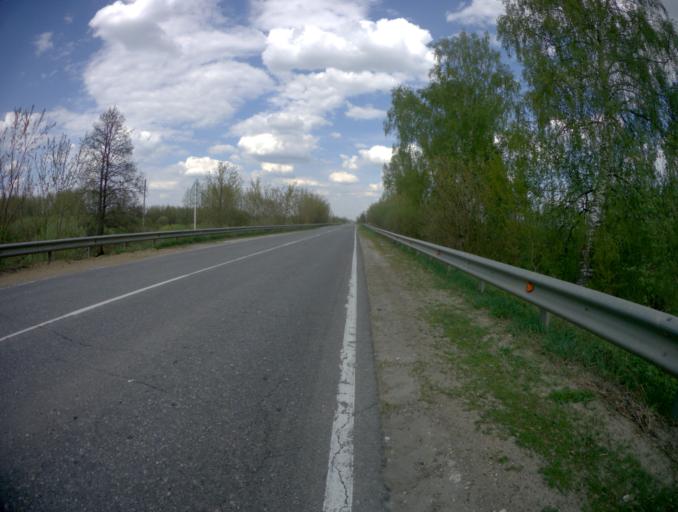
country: RU
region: Vladimir
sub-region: Kovrovskiy Rayon
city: Kovrov
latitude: 56.4374
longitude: 41.2621
